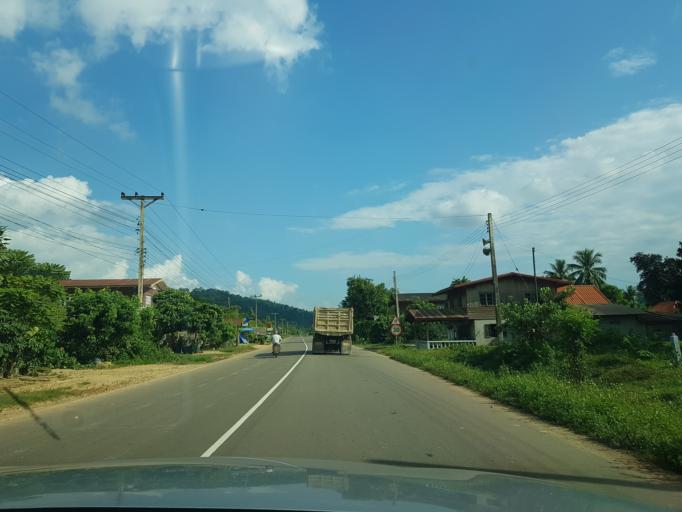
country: TH
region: Nong Khai
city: Sangkhom
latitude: 18.0195
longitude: 102.3924
